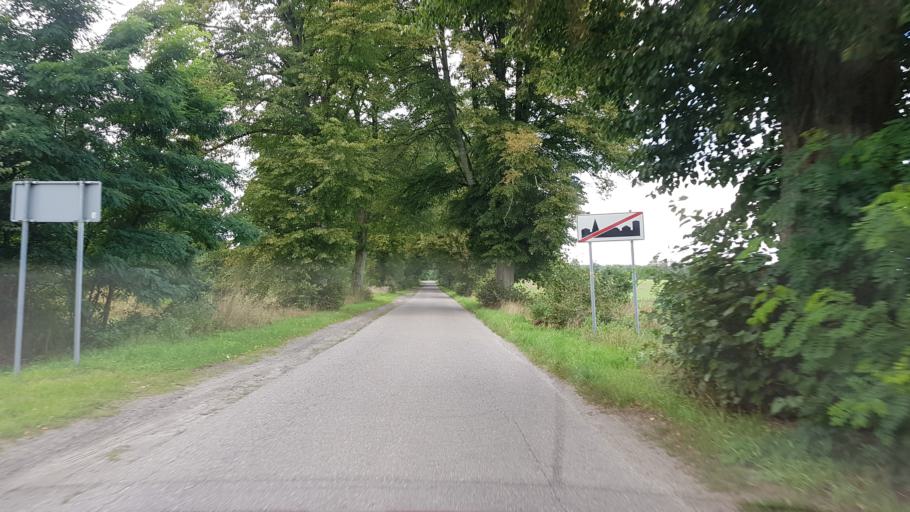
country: PL
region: West Pomeranian Voivodeship
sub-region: Powiat bialogardzki
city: Tychowo
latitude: 54.0247
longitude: 16.3581
